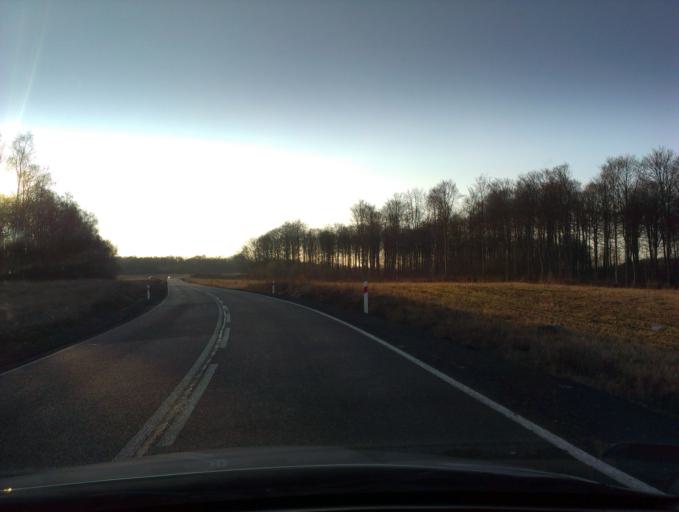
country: PL
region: West Pomeranian Voivodeship
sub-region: Powiat szczecinecki
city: Borne Sulinowo
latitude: 53.6212
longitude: 16.5295
